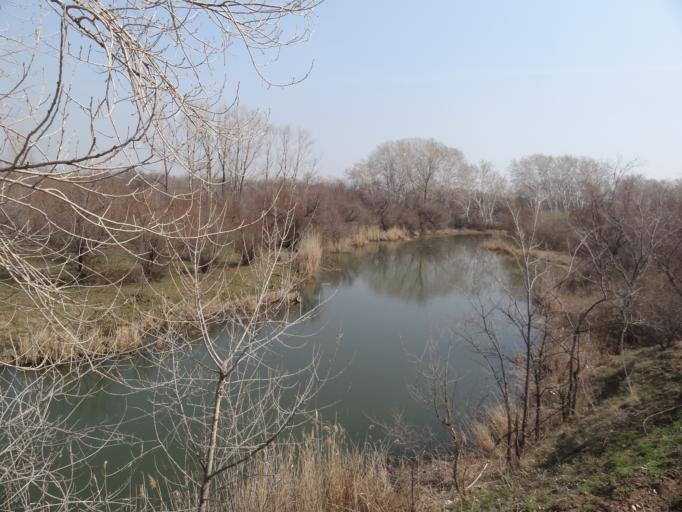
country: RU
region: Saratov
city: Privolzhskiy
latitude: 51.2958
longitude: 45.9589
